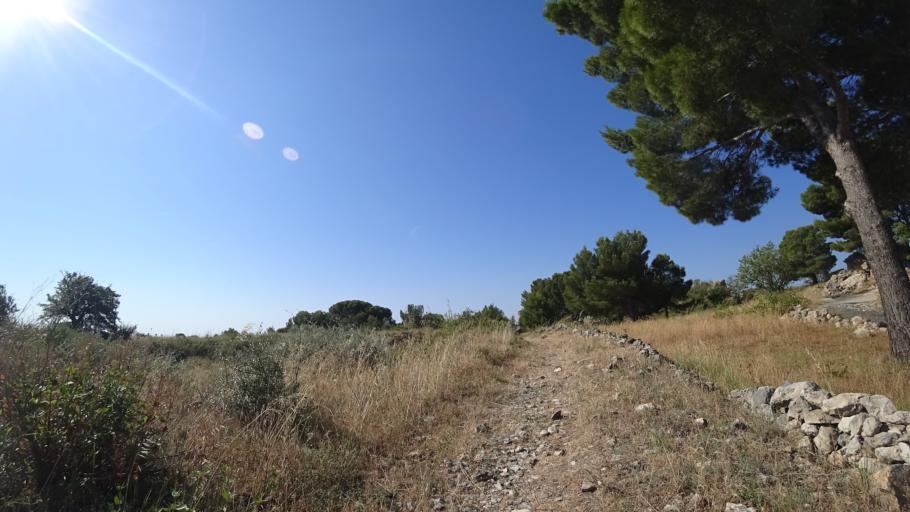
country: FR
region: Languedoc-Roussillon
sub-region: Departement de l'Aude
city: Leucate
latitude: 42.9084
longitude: 3.0261
